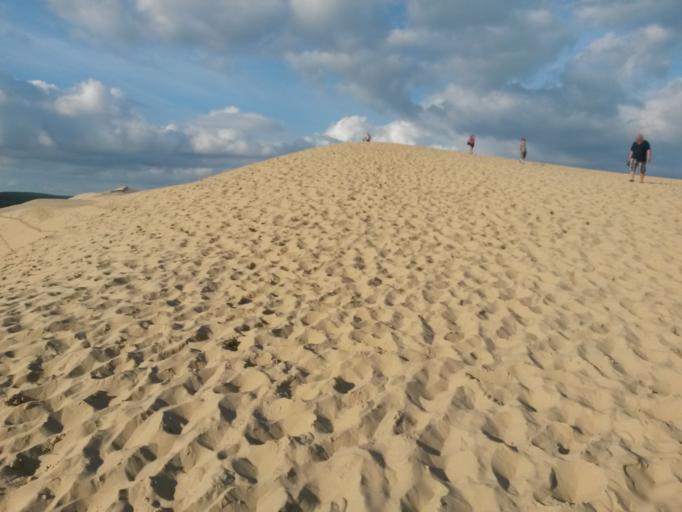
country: FR
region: Aquitaine
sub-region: Departement de la Gironde
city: Arcachon
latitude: 44.5989
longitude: -1.2052
